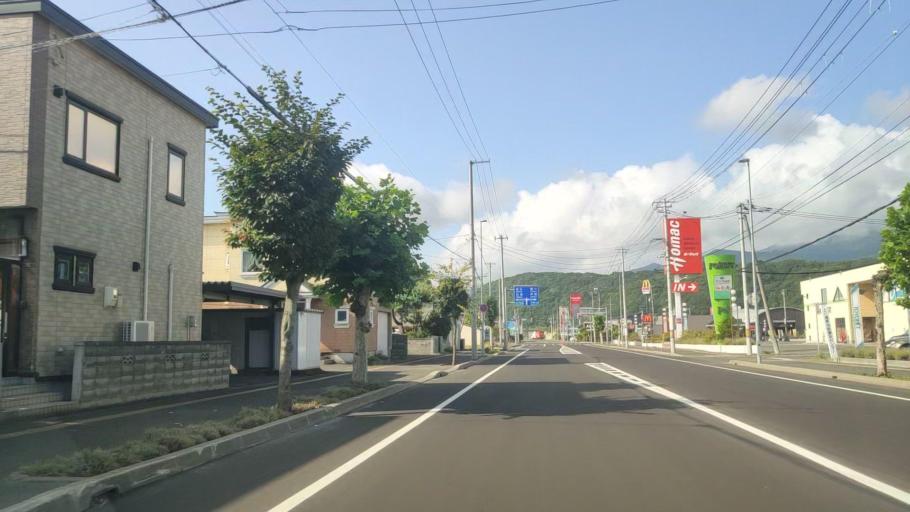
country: JP
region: Hokkaido
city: Shimo-furano
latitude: 43.3457
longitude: 142.3823
